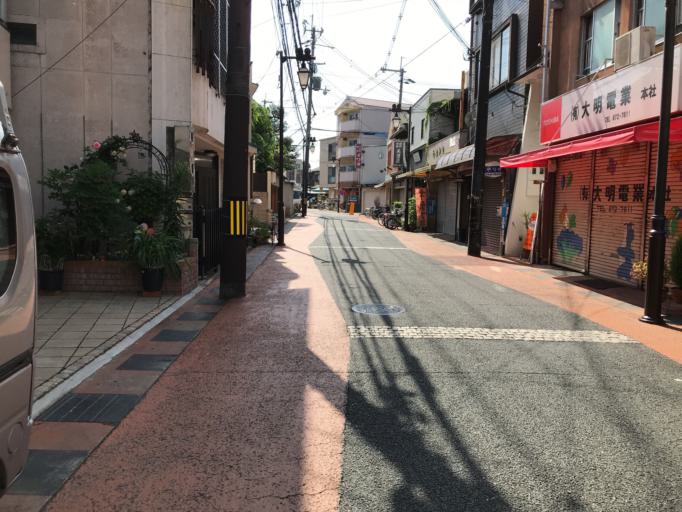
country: JP
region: Kyoto
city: Muko
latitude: 35.0141
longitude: 135.7018
